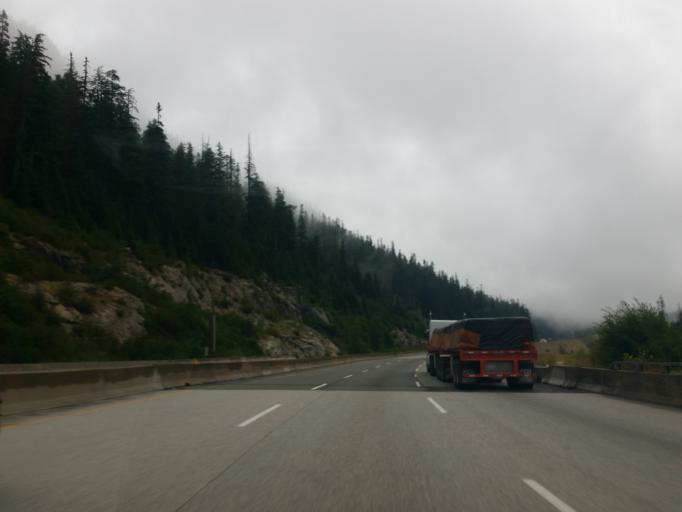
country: CA
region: British Columbia
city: Hope
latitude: 49.5966
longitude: -121.1589
